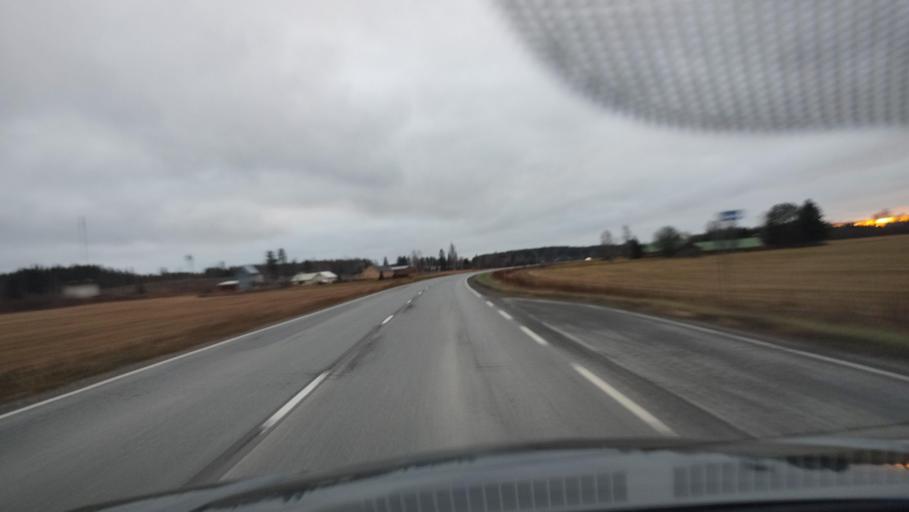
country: FI
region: Southern Ostrobothnia
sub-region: Suupohja
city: Kauhajoki
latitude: 62.3619
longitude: 22.0721
